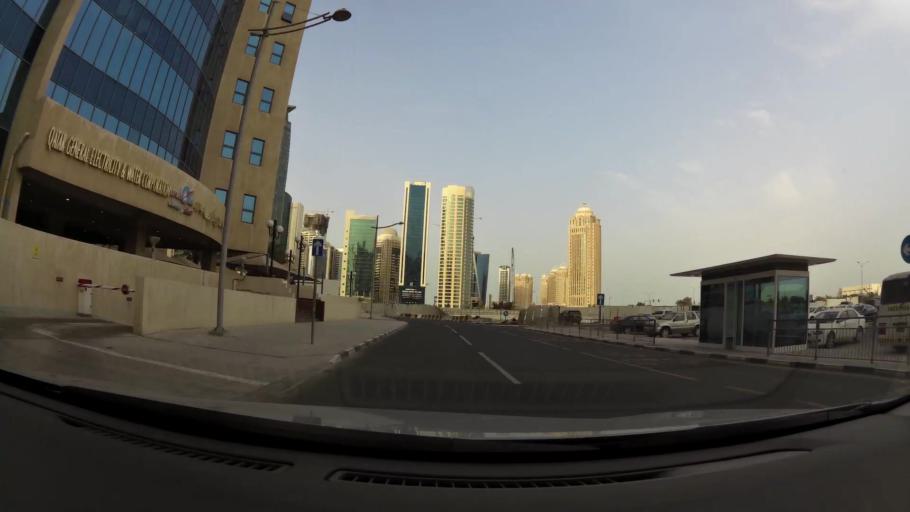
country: QA
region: Baladiyat ad Dawhah
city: Doha
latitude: 25.3211
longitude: 51.5323
